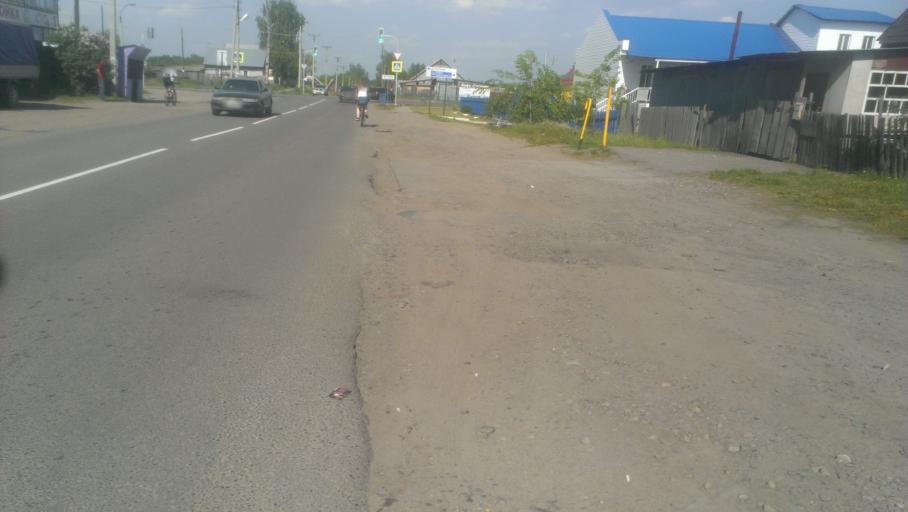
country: RU
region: Altai Krai
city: Novoaltaysk
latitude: 53.4016
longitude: 83.9451
